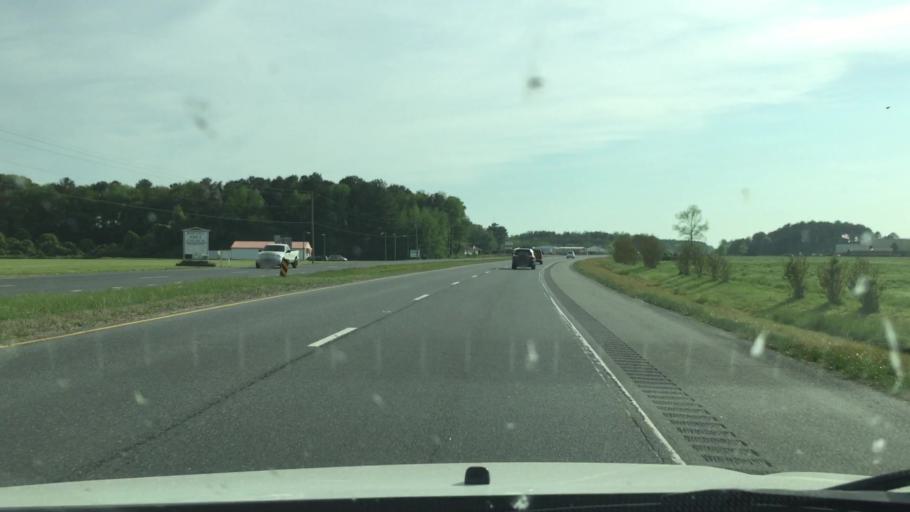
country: US
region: Virginia
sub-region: Accomack County
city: Accomac
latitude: 37.7351
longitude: -75.6494
